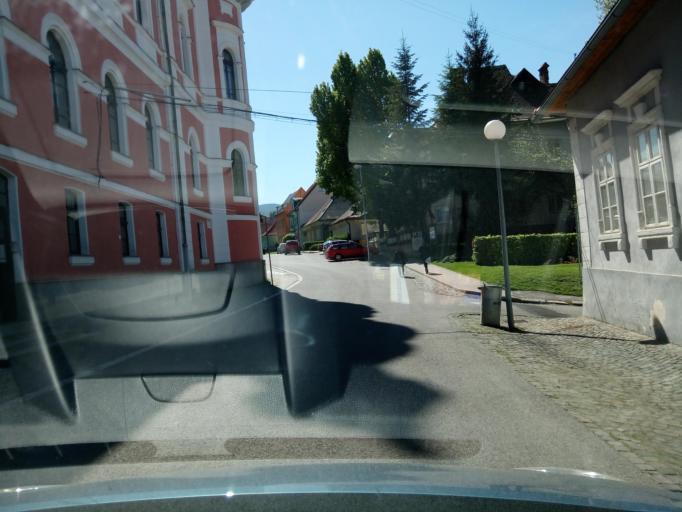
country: SK
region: Zilinsky
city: Ruzomberok
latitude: 49.0818
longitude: 19.3037
